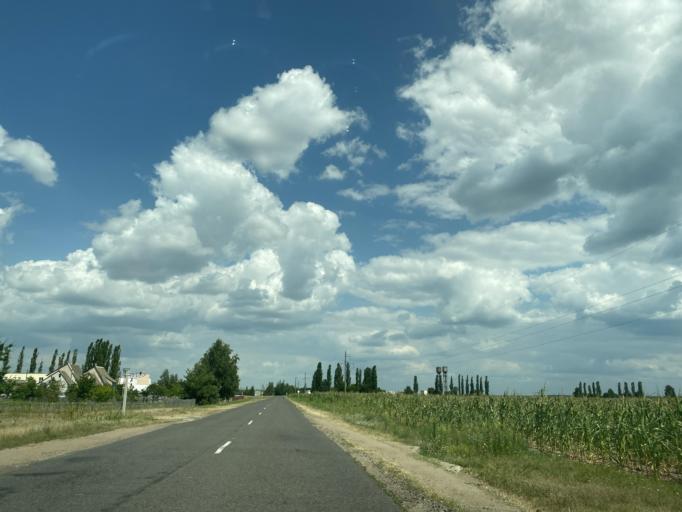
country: BY
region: Brest
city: Ivanava
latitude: 52.3432
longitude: 25.6263
